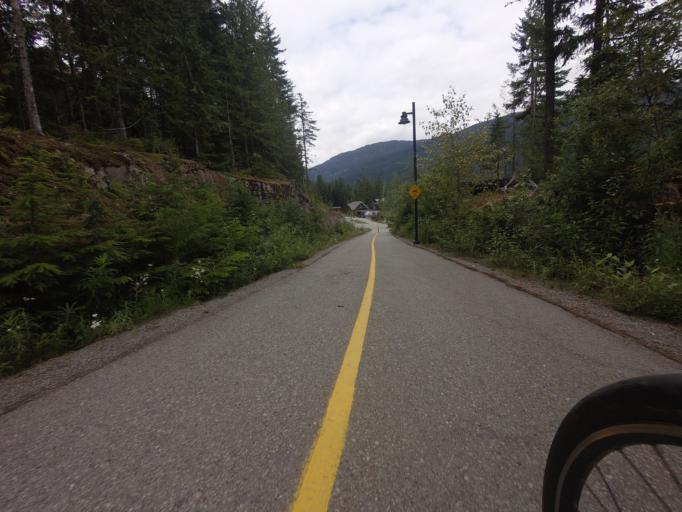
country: CA
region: British Columbia
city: Whistler
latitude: 50.0867
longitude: -123.0120
